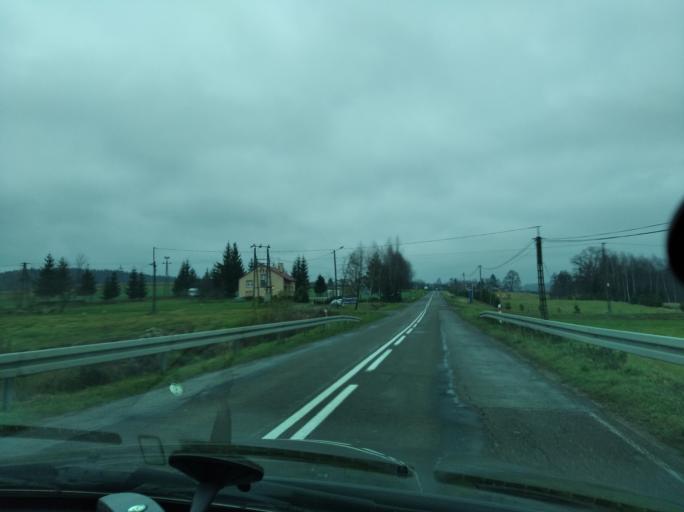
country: PL
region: Subcarpathian Voivodeship
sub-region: Powiat rzeszowski
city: Dynow
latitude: 49.8586
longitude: 22.2493
